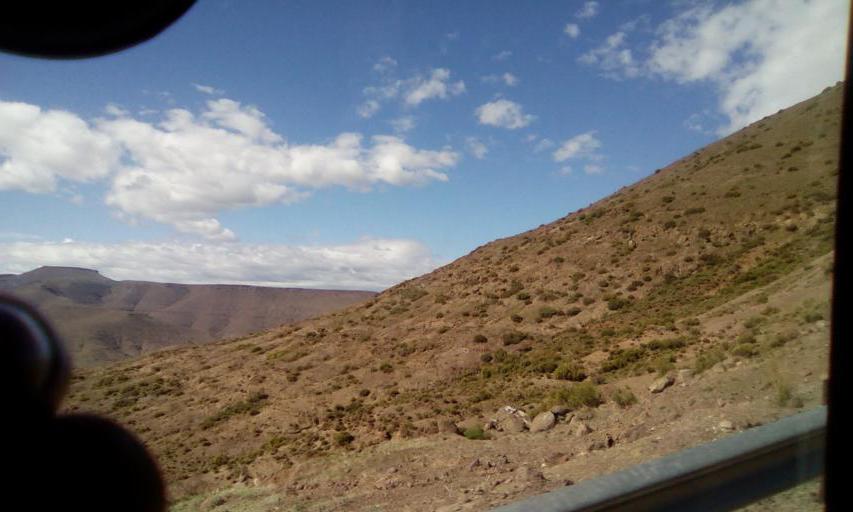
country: LS
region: Qacha's Nek
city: Qacha's Nek
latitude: -30.0094
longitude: 28.1723
